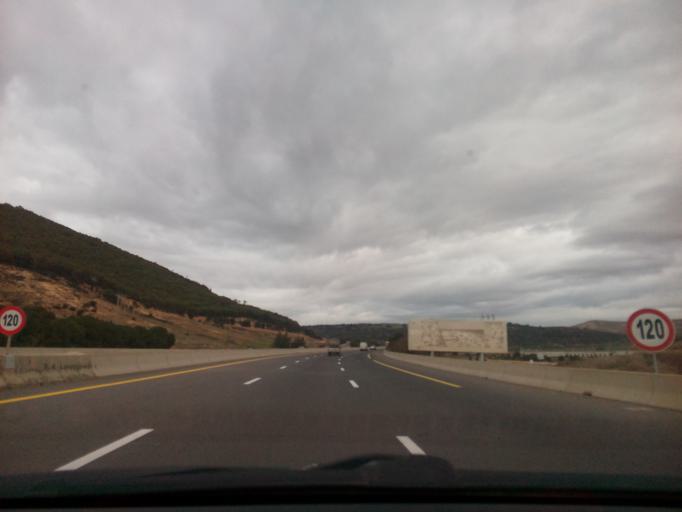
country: DZ
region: Sidi Bel Abbes
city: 'Ain el Berd
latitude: 35.3851
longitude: -0.4971
